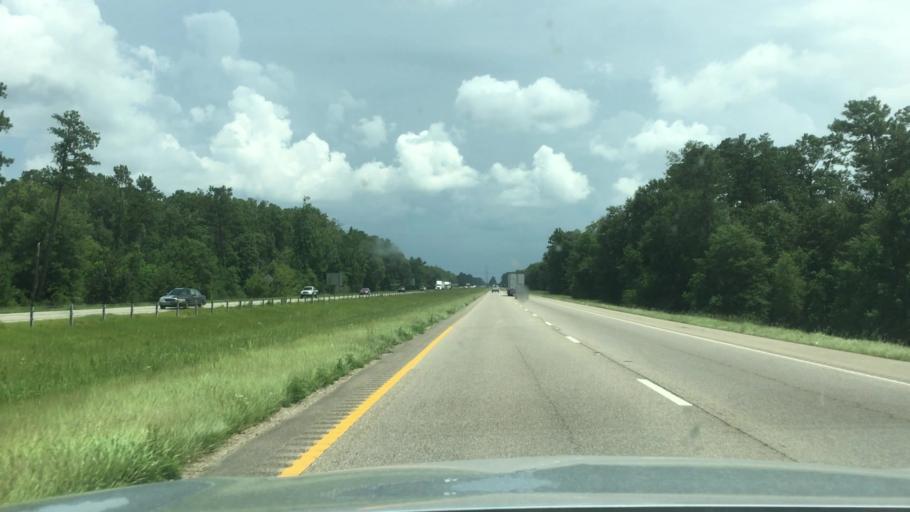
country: US
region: Mississippi
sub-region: Pearl River County
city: Picayune
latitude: 30.5296
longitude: -89.6571
